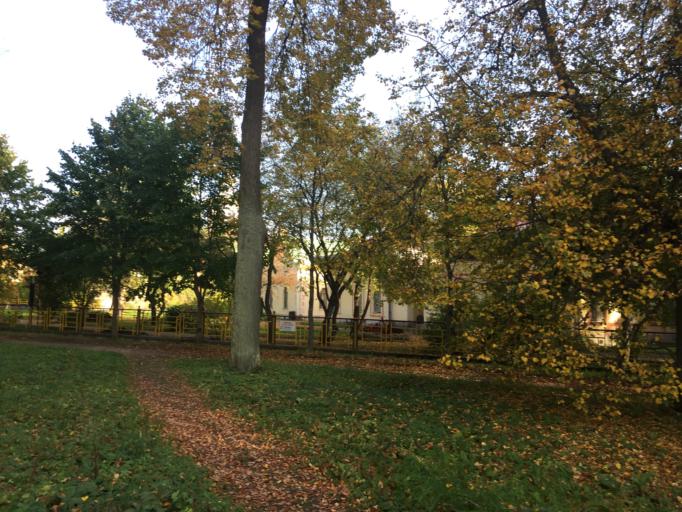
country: RU
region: St.-Petersburg
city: Pushkin
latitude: 59.7145
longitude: 30.3842
